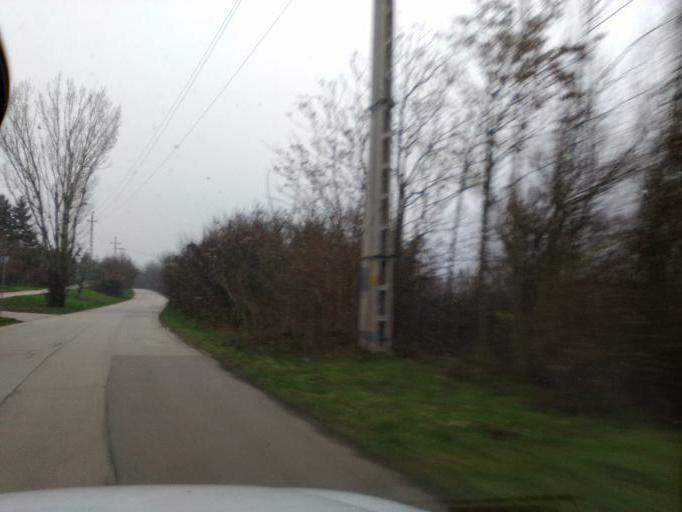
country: HU
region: Pest
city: Soskut
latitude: 47.3989
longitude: 18.7883
